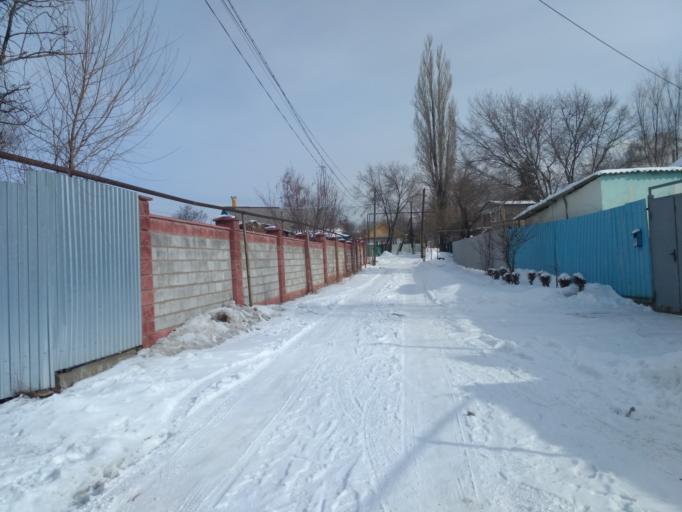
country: KZ
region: Almaty Oblysy
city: Burunday
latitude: 43.1586
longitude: 76.4069
